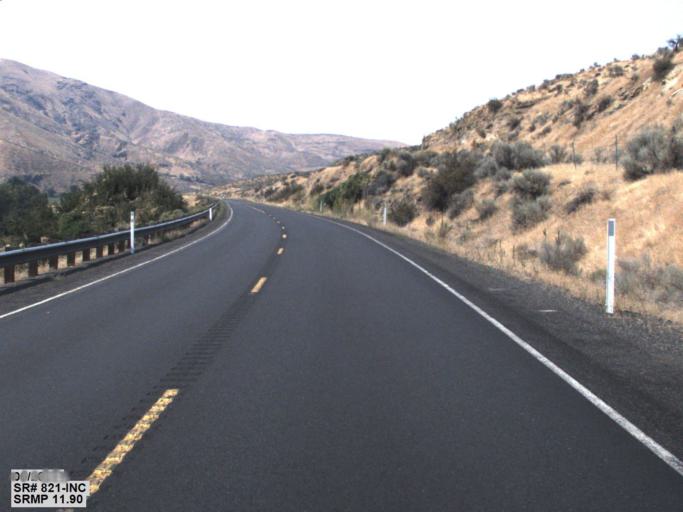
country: US
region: Washington
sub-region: Kittitas County
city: Kittitas
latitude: 46.8104
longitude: -120.4425
